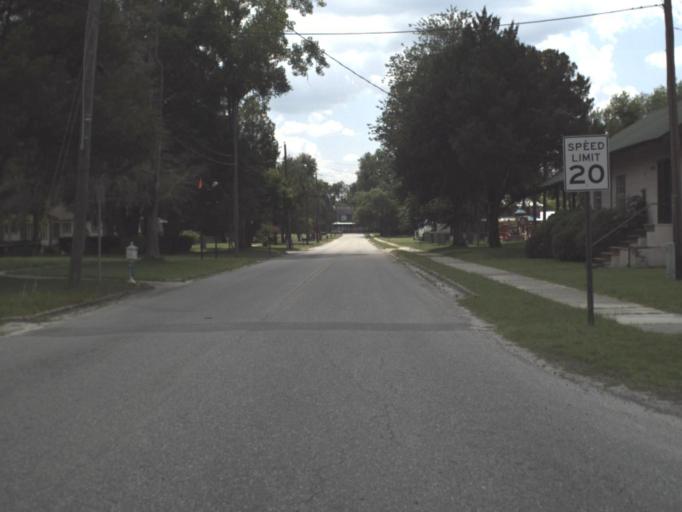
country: US
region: Florida
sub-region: Bradford County
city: Starke
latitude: 30.0445
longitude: -82.0725
